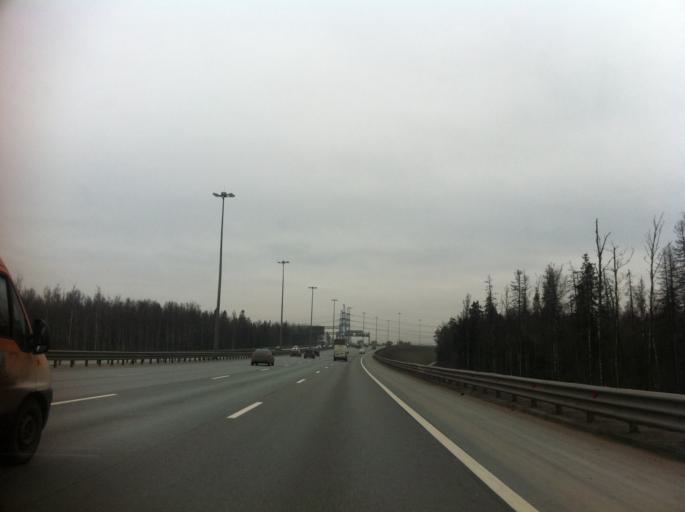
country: RU
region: St.-Petersburg
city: Krasnogvargeisky
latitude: 59.9368
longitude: 30.5382
